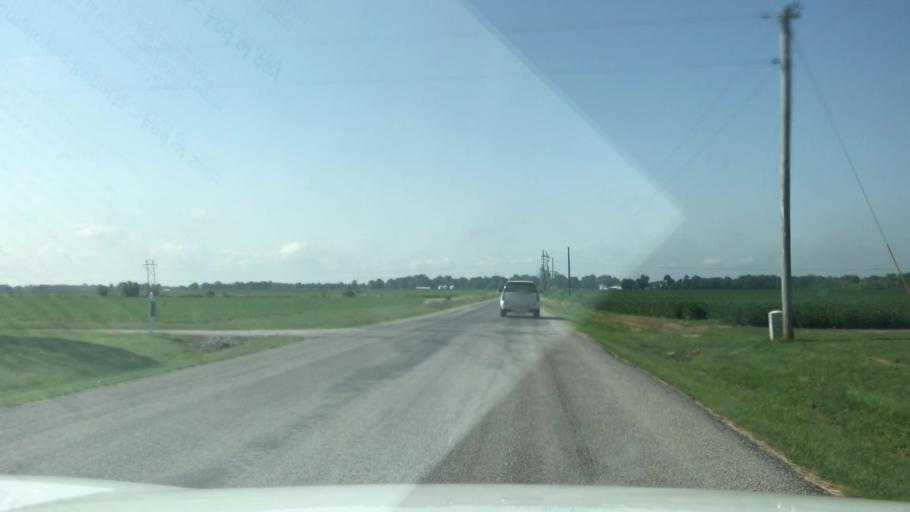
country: US
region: Illinois
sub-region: Washington County
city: Okawville
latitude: 38.4058
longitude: -89.4866
